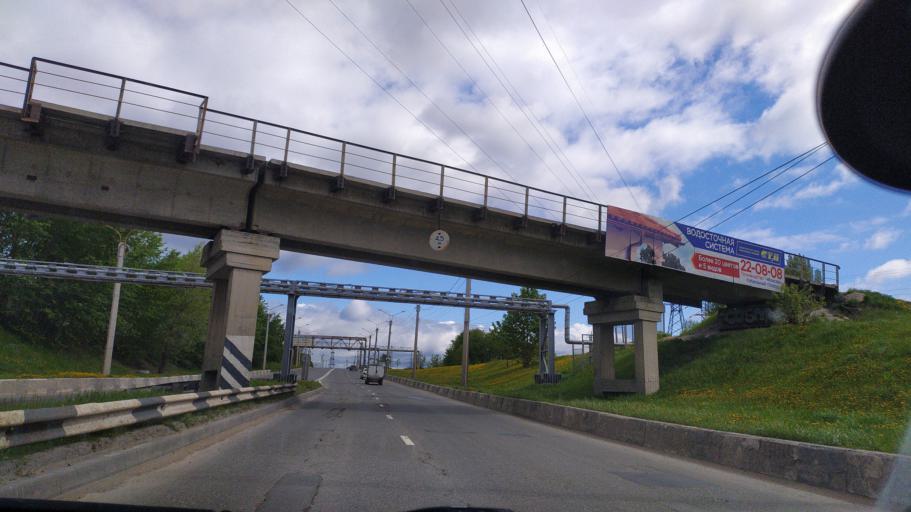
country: RU
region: Chuvashia
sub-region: Cheboksarskiy Rayon
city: Cheboksary
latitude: 56.1128
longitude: 47.2971
